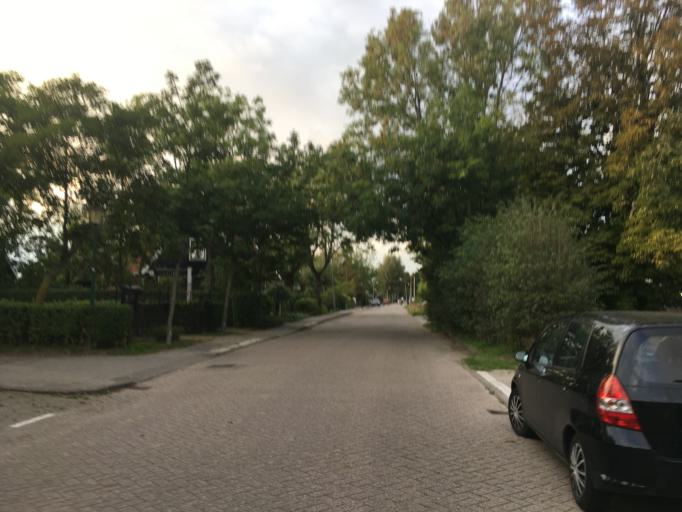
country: NL
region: North Holland
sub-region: Gemeente Zaanstad
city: Zaanstad
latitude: 52.4406
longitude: 4.7783
